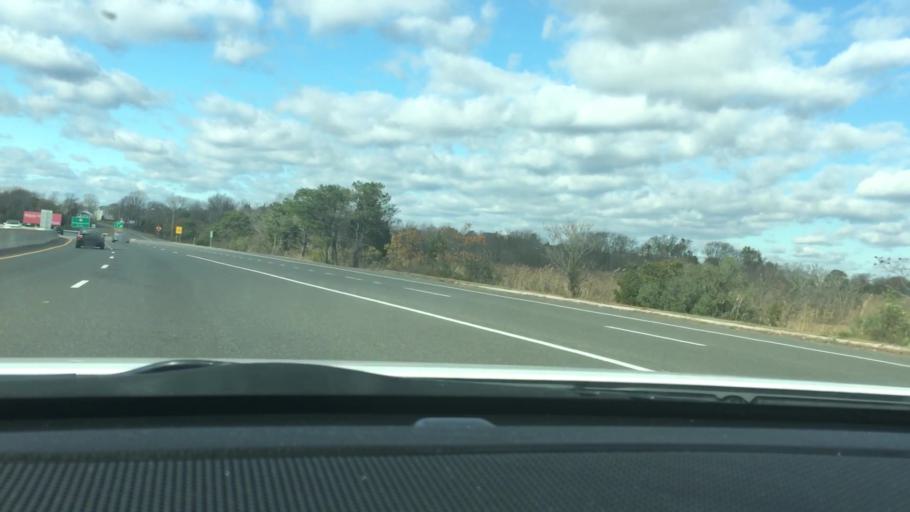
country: US
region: New Jersey
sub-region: Atlantic County
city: Pleasantville
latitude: 39.3940
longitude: -74.5112
